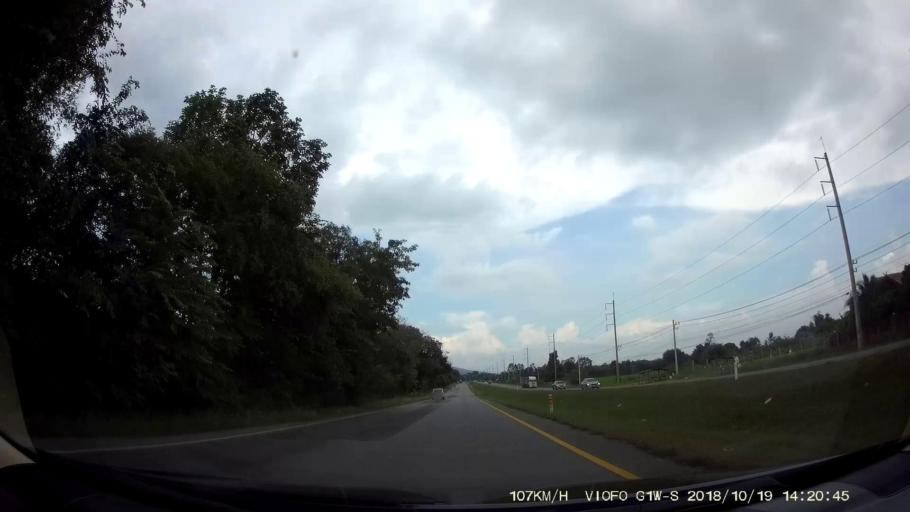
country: TH
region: Chaiyaphum
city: Kaeng Khro
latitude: 16.0443
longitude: 102.2591
